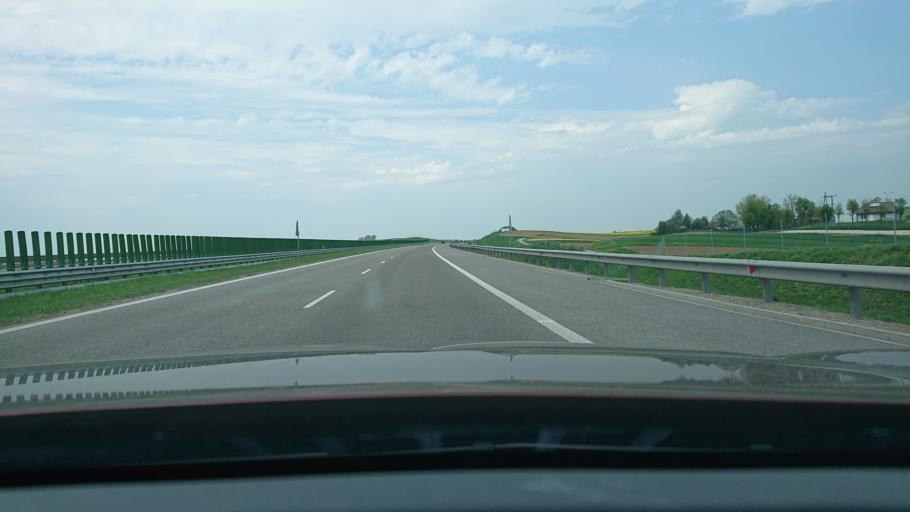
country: PL
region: Subcarpathian Voivodeship
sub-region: Powiat jaroslawski
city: Pawlosiow
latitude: 49.9497
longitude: 22.6639
